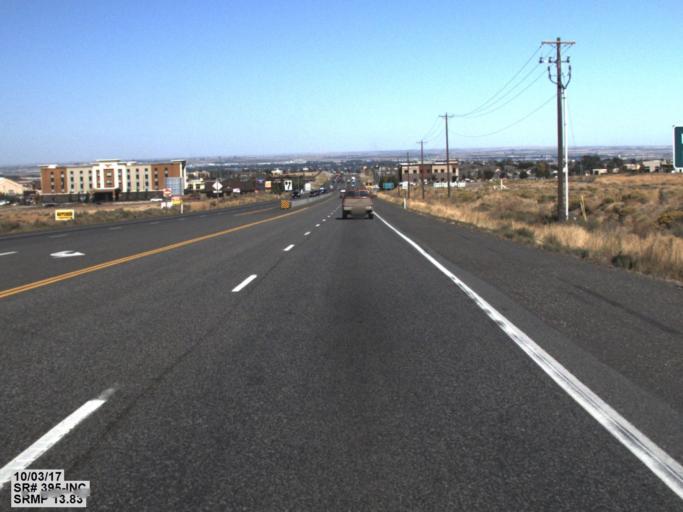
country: US
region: Washington
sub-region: Benton County
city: Kennewick
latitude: 46.1734
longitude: -119.1918
